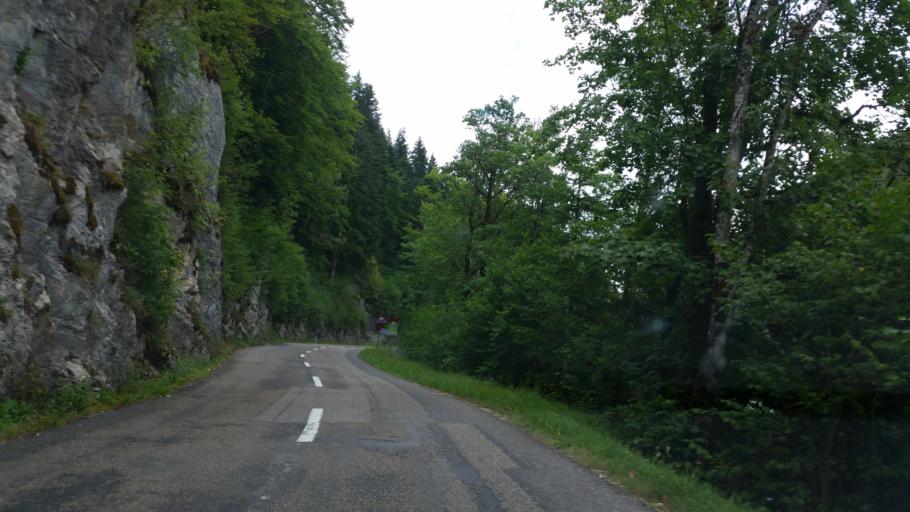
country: CH
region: Jura
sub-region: Franches-Montagnes District
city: Les Bois
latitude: 47.1623
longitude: 6.8566
